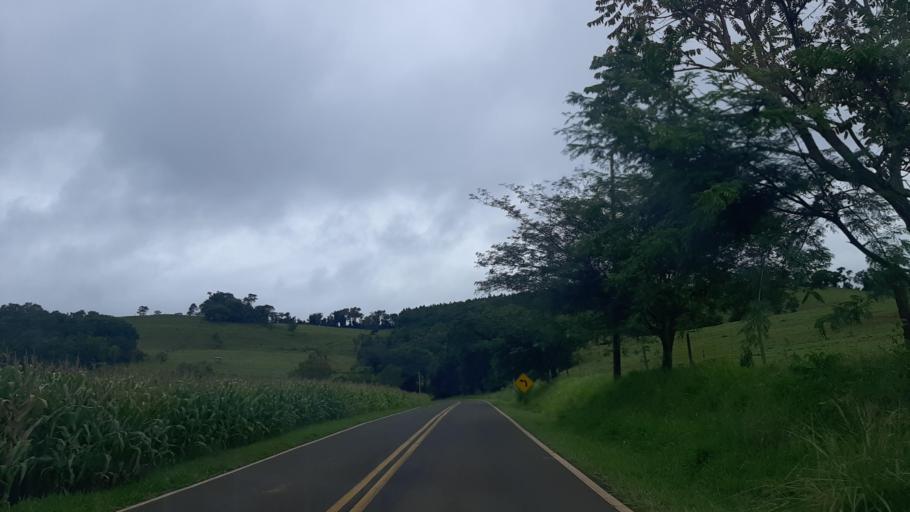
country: BR
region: Parana
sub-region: Ampere
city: Ampere
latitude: -25.9822
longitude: -53.4440
